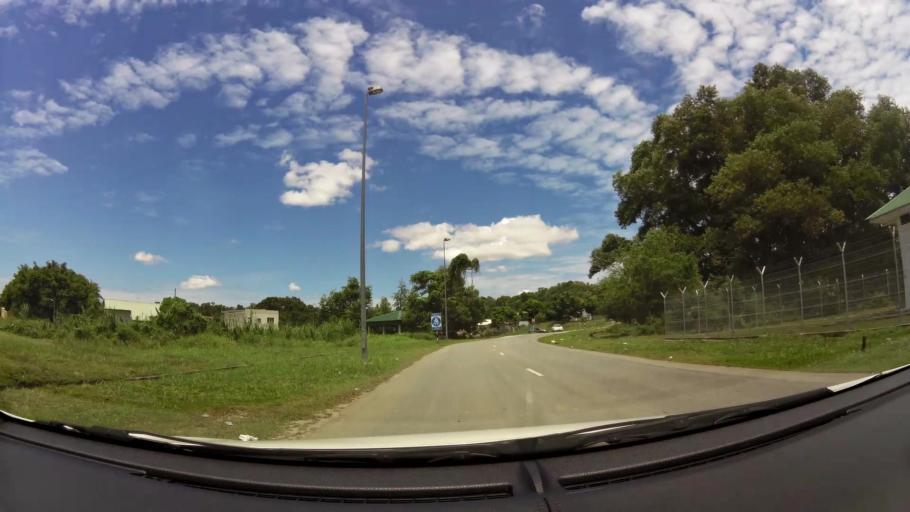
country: BN
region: Brunei and Muara
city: Bandar Seri Begawan
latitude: 4.9956
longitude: 115.0246
